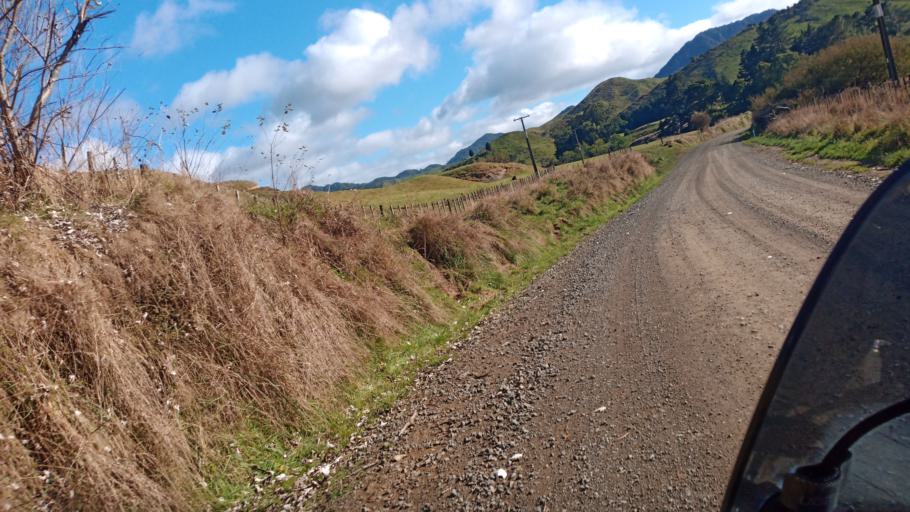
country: NZ
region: Bay of Plenty
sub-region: Opotiki District
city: Opotiki
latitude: -38.4667
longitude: 177.4273
